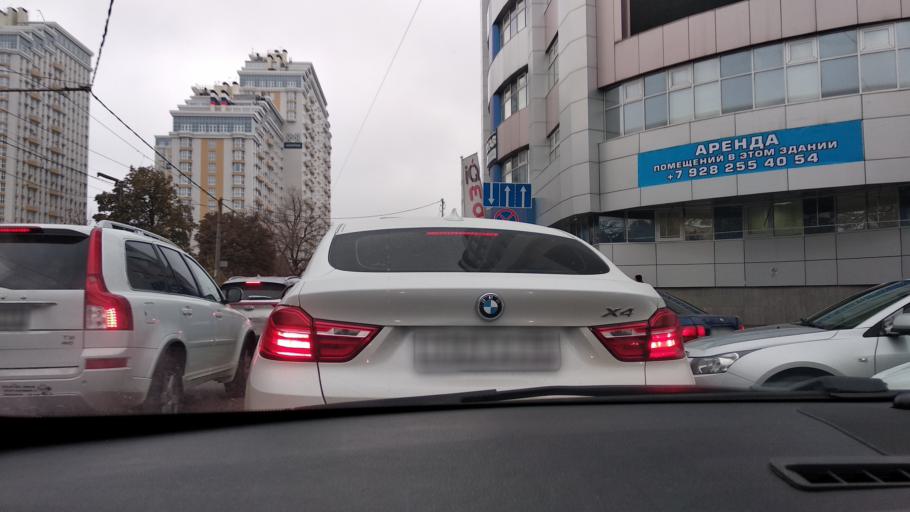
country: RU
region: Krasnodarskiy
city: Krasnodar
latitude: 45.0440
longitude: 38.9815
